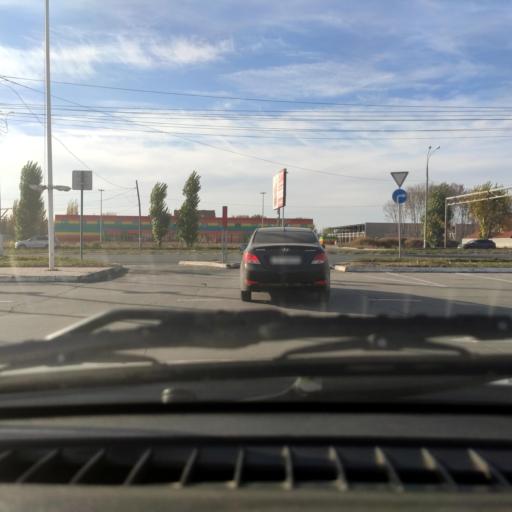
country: RU
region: Samara
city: Tol'yatti
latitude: 53.5437
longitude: 49.2860
